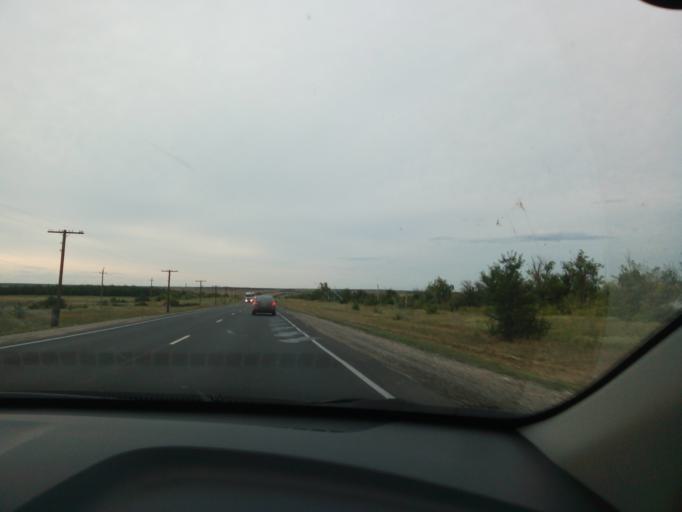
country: RU
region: Volgograd
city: Dubovka
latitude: 49.1135
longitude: 44.8114
